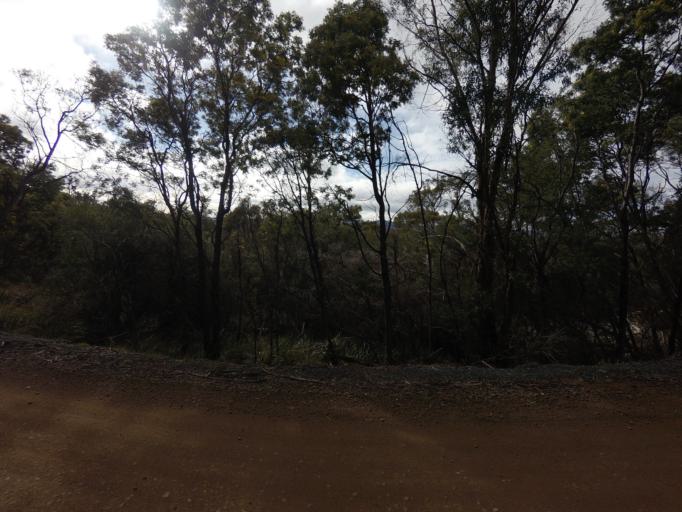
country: AU
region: Tasmania
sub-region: Derwent Valley
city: New Norfolk
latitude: -42.7296
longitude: 146.8661
